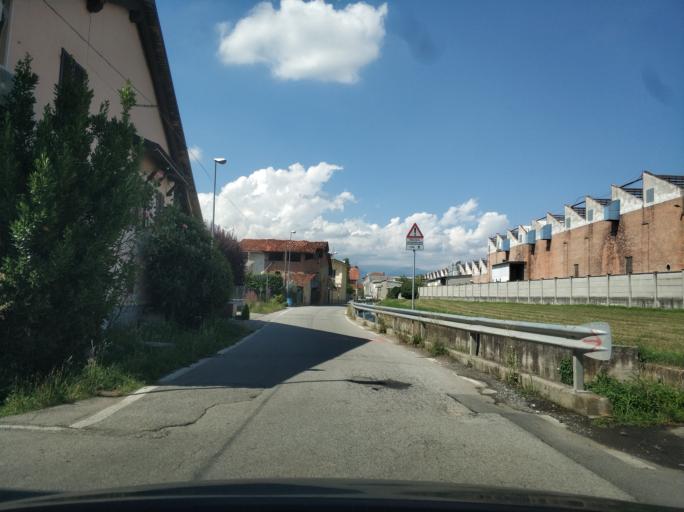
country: IT
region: Piedmont
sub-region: Provincia di Torino
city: Rivarolo Canavese
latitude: 45.3149
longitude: 7.7227
